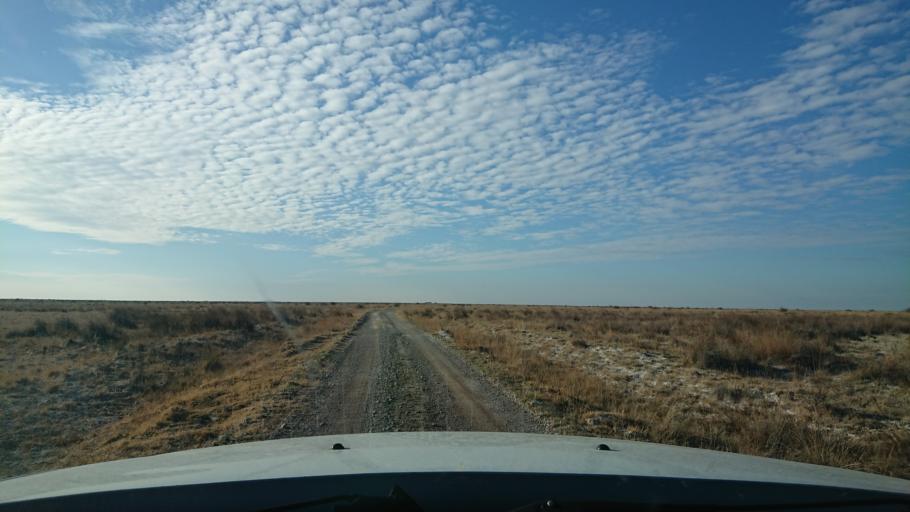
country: TR
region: Aksaray
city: Eskil
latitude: 38.5399
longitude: 33.3394
